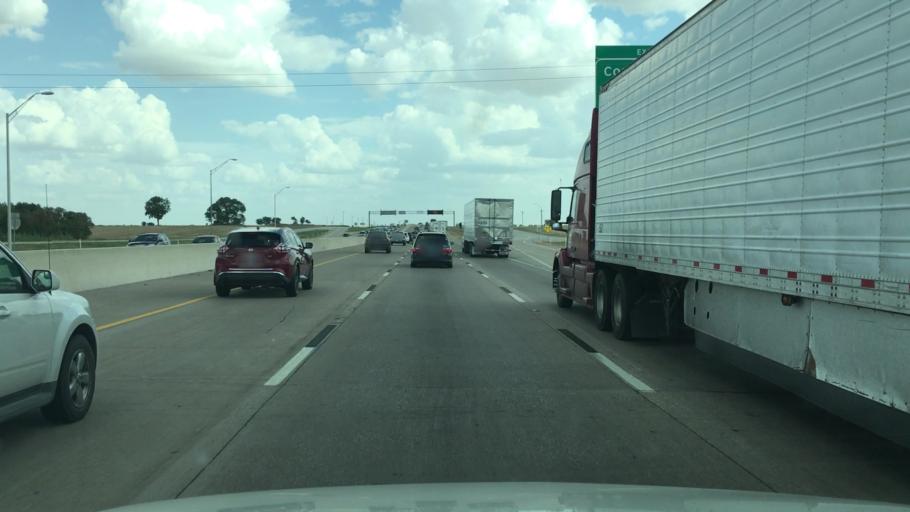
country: US
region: Texas
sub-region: Hill County
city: Hillsboro
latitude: 31.9528
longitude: -97.1137
